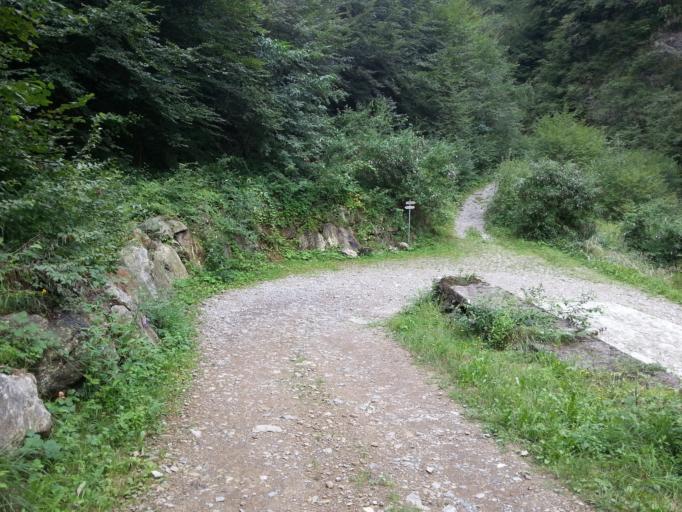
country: IT
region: Lombardy
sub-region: Provincia di Lecco
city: Cortenova
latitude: 45.9910
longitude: 9.3838
